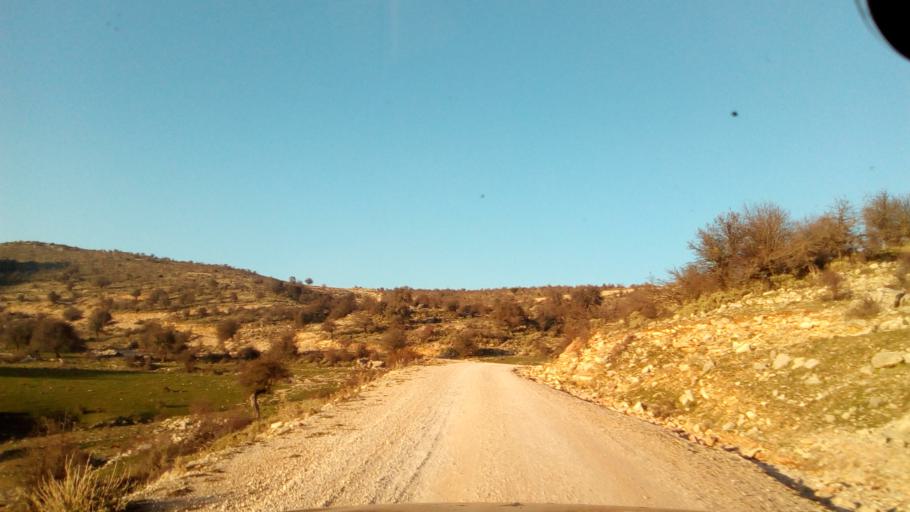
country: GR
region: West Greece
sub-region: Nomos Aitolias kai Akarnanias
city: Nafpaktos
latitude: 38.4540
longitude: 21.8437
